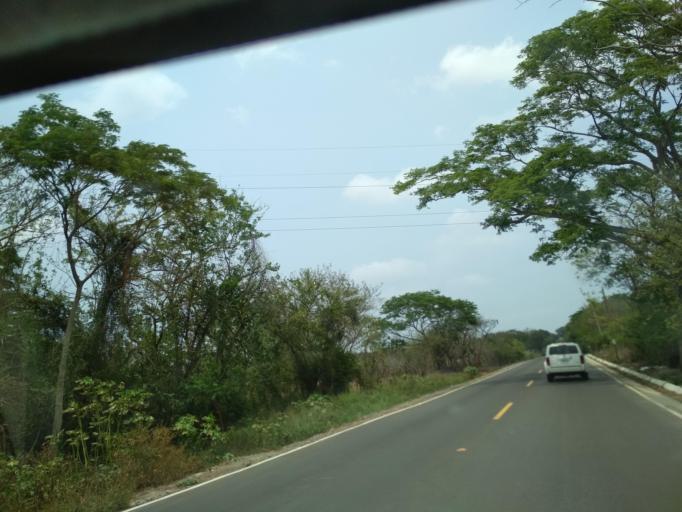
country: MX
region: Veracruz
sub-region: Veracruz
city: Delfino Victoria (Santa Fe)
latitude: 19.1709
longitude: -96.2810
